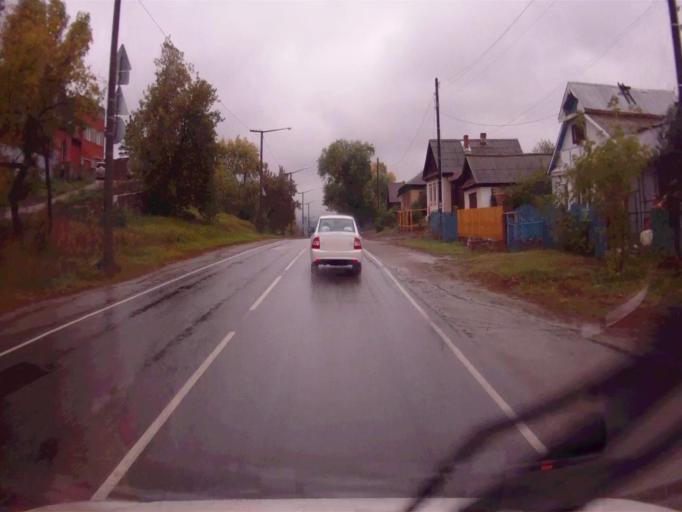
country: RU
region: Chelyabinsk
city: Kyshtym
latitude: 55.7221
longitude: 60.5320
